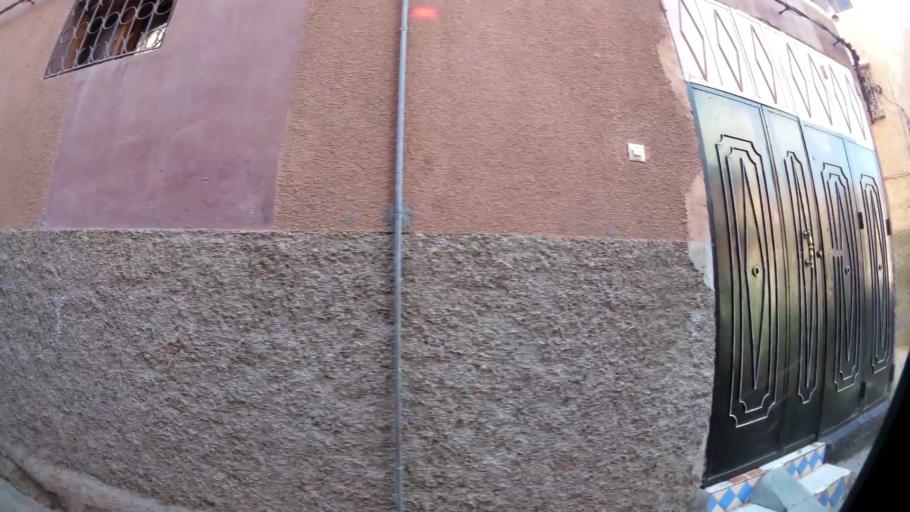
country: MA
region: Marrakech-Tensift-Al Haouz
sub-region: Marrakech
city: Marrakesh
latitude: 31.6161
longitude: -7.9666
